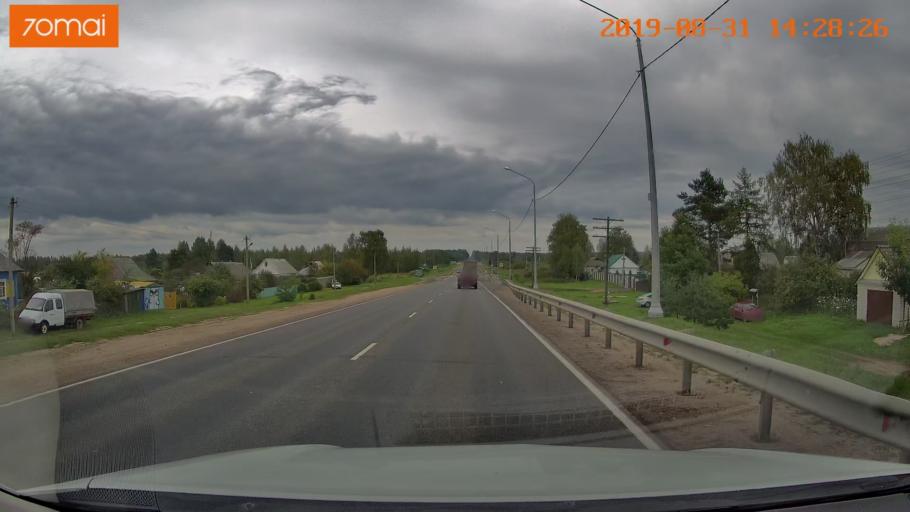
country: RU
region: Smolensk
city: Yekimovichi
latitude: 54.1202
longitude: 33.3132
